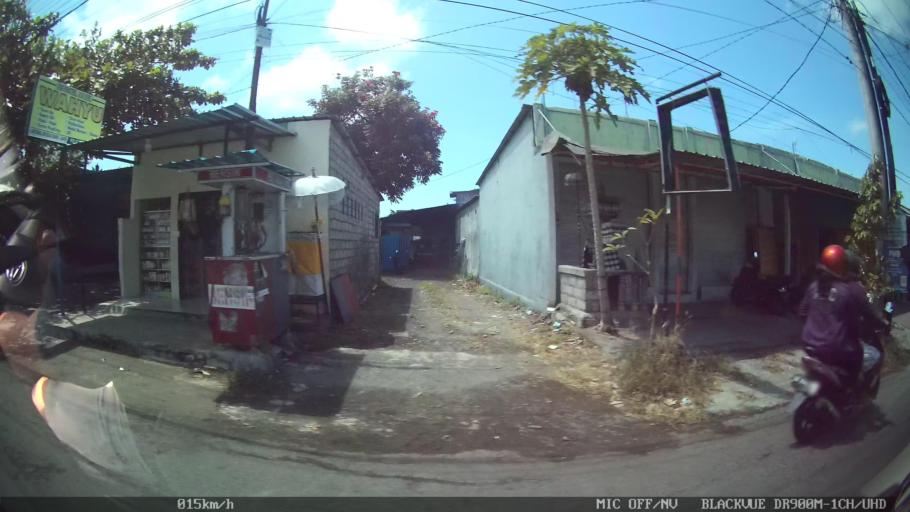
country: ID
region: Bali
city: Banjar Jabejero
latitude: -8.6102
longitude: 115.2586
